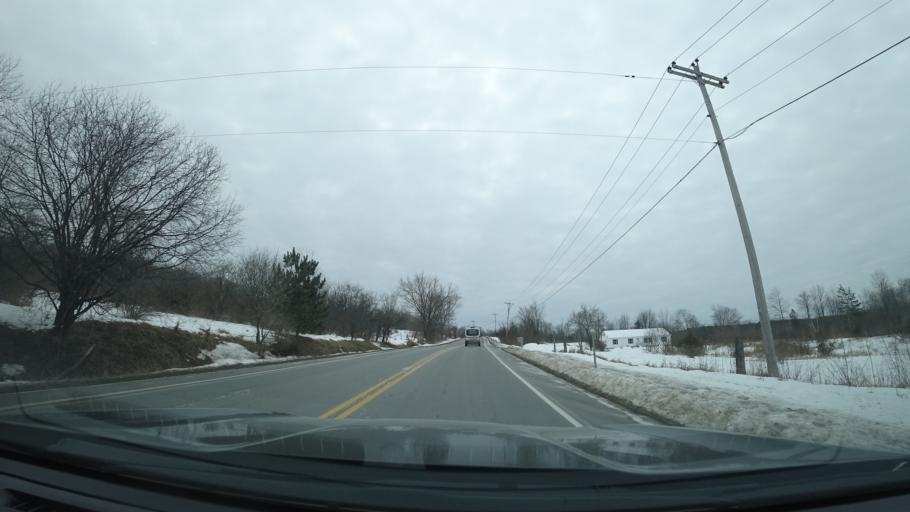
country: US
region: New York
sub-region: Washington County
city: Fort Edward
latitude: 43.2538
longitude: -73.5029
